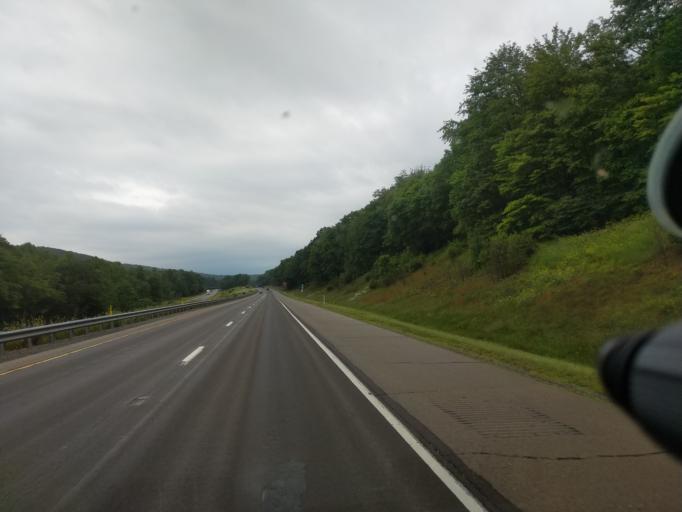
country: US
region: Pennsylvania
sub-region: Union County
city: Mifflinburg
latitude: 41.0449
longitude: -77.1216
